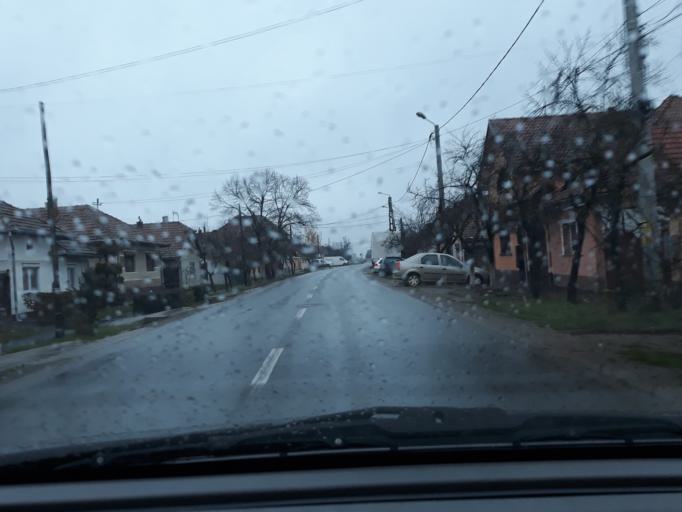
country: RO
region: Bihor
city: Margita
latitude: 47.3518
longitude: 22.3500
